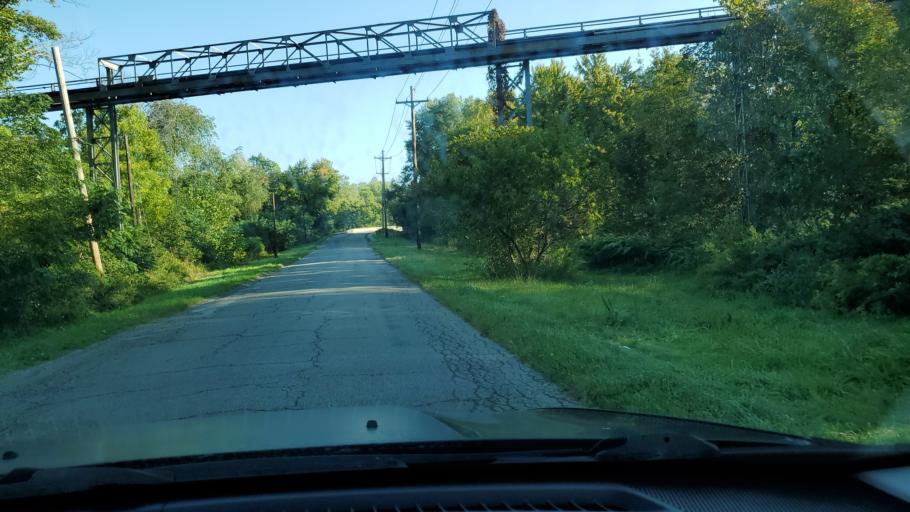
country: US
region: Ohio
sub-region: Trumbull County
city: Niles
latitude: 41.1690
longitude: -80.7531
